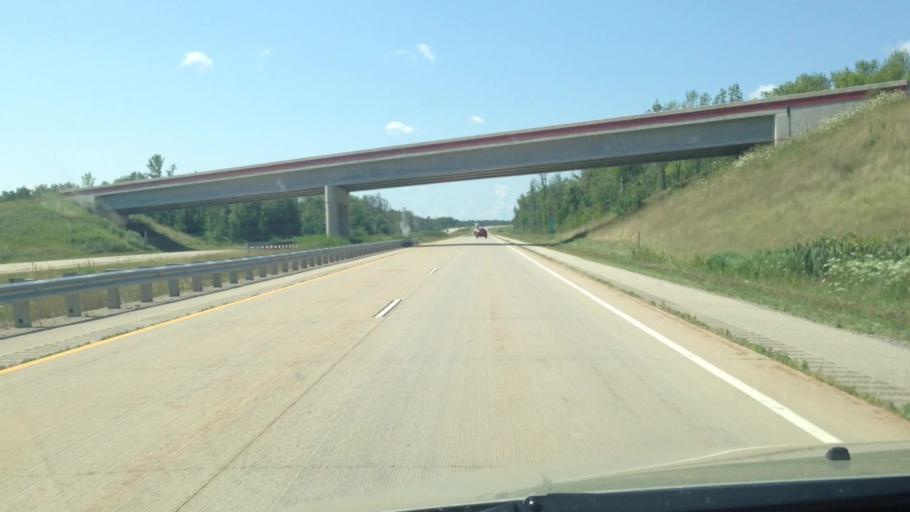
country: US
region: Wisconsin
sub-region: Oconto County
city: Oconto
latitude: 44.9179
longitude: -87.8750
